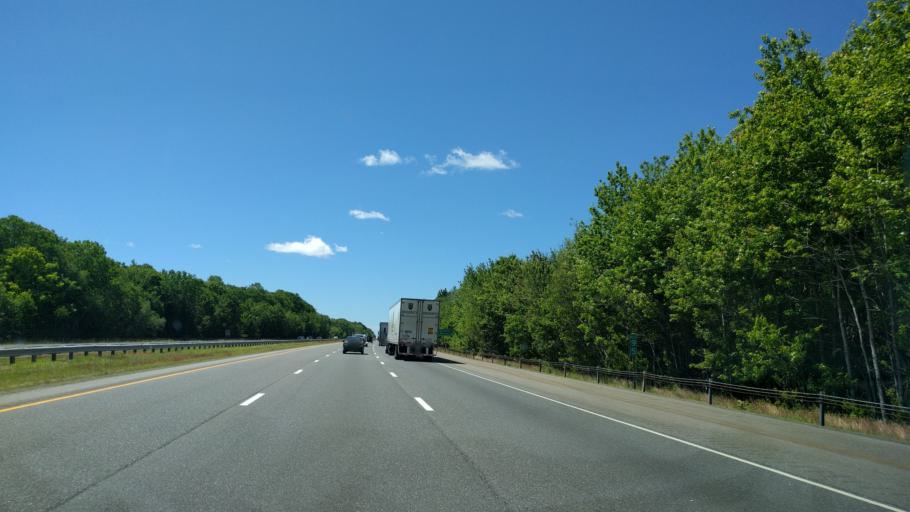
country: US
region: Massachusetts
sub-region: Hampden County
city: Holland
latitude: 41.9971
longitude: -72.1674
